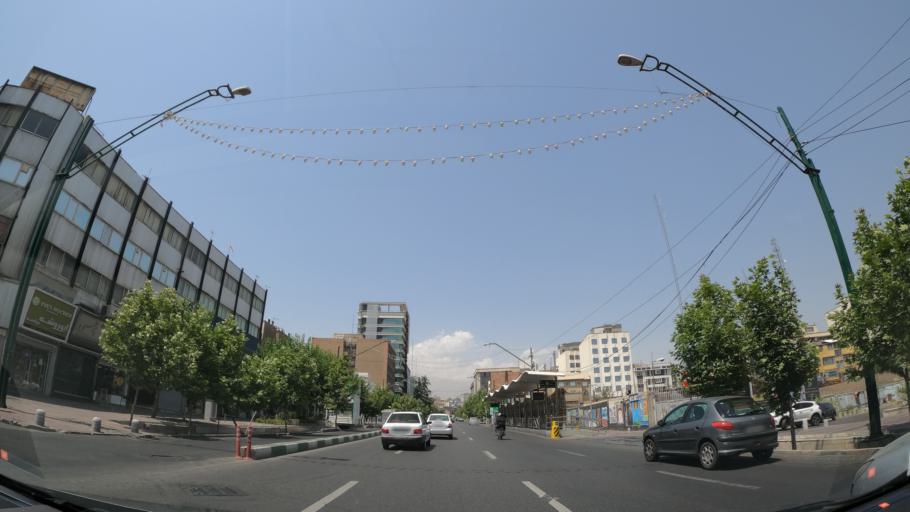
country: IR
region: Tehran
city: Tehran
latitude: 35.7235
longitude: 51.4139
